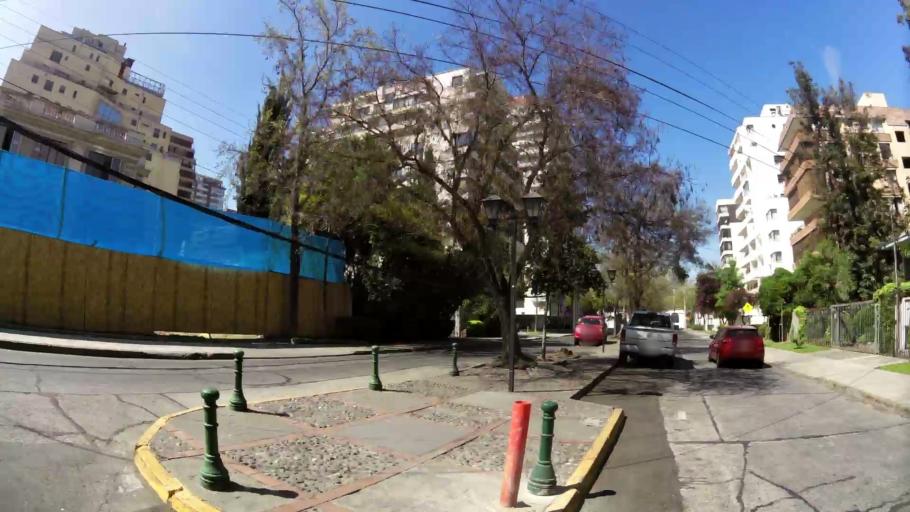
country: CL
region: Santiago Metropolitan
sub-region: Provincia de Santiago
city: Villa Presidente Frei, Nunoa, Santiago, Chile
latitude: -33.4127
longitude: -70.5783
